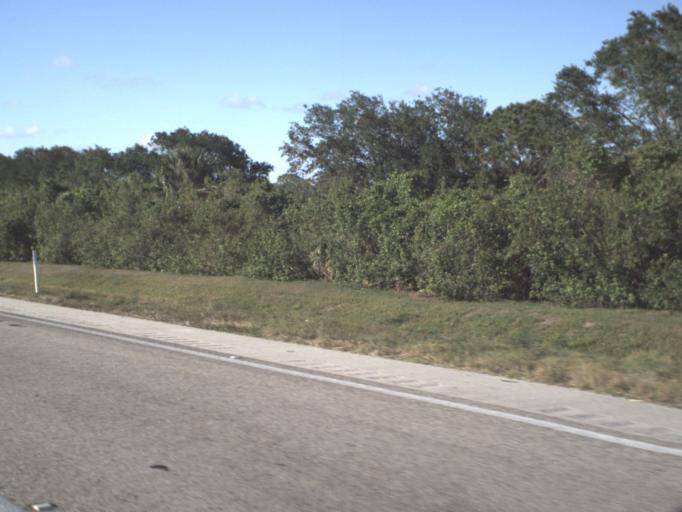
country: US
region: Florida
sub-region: Brevard County
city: Rockledge
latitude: 28.2372
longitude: -80.7203
